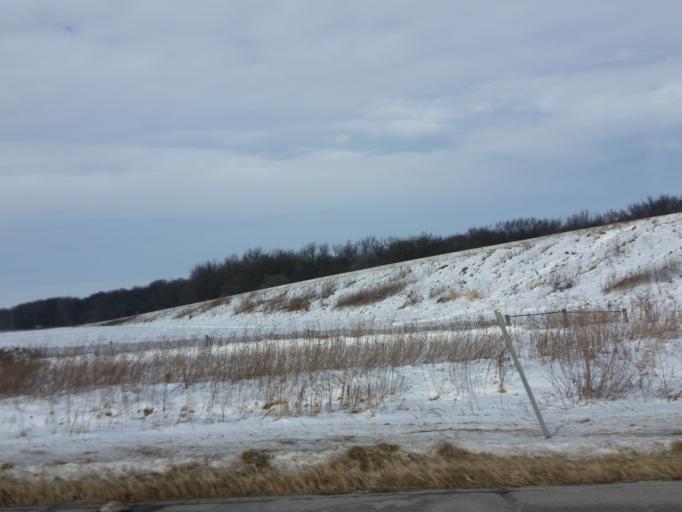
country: US
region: Iowa
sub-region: Buchanan County
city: Independence
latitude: 42.4608
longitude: -91.7125
